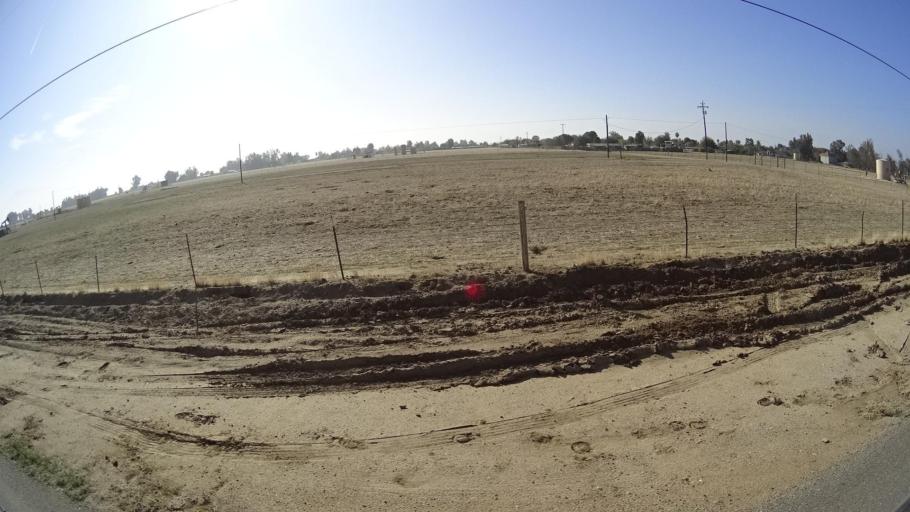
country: US
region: California
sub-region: Kern County
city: Lamont
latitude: 35.3398
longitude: -118.9072
